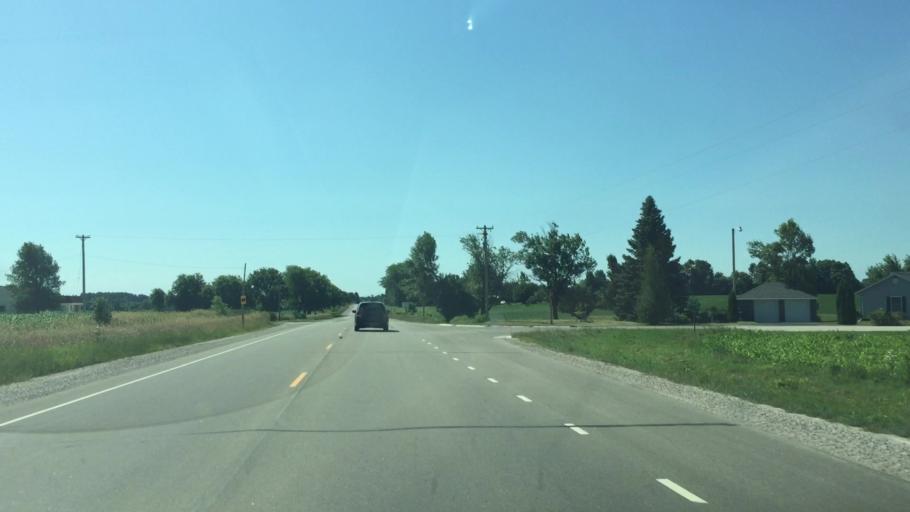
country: US
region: Wisconsin
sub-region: Calumet County
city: New Holstein
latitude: 43.9869
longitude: -88.1199
